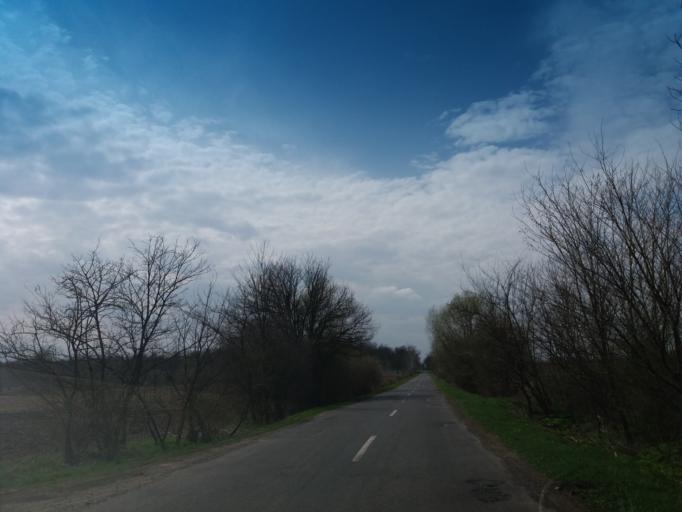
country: HU
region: Szabolcs-Szatmar-Bereg
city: Petnehaza
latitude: 48.0550
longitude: 22.0547
